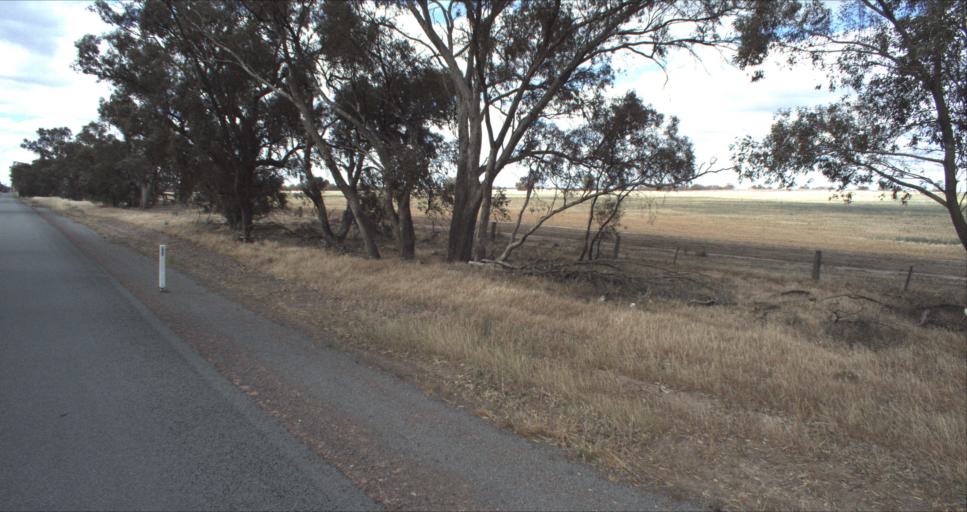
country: AU
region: New South Wales
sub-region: Leeton
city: Leeton
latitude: -34.6808
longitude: 146.3456
